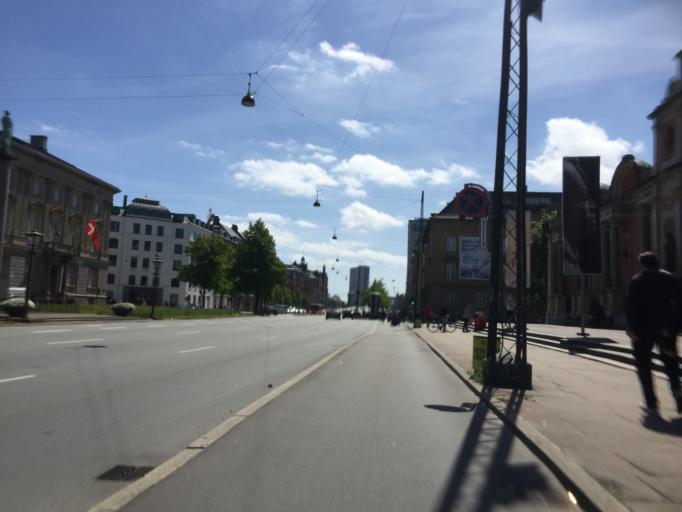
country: DK
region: Capital Region
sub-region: Kobenhavn
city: Copenhagen
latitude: 55.6733
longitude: 12.5724
